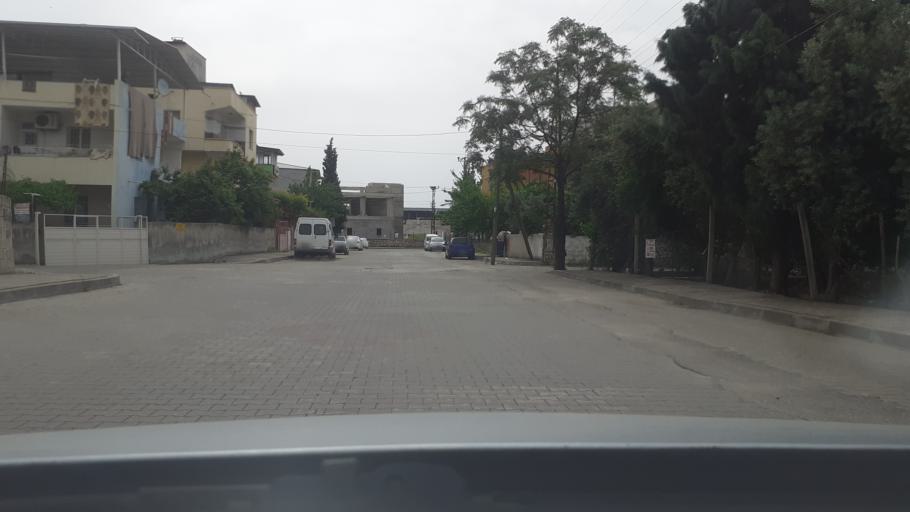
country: TR
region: Hatay
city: Kirikhan
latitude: 36.4941
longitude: 36.3661
